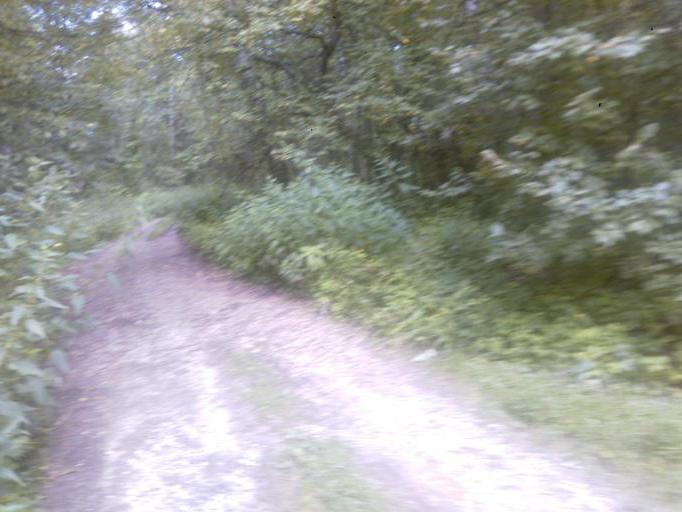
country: RU
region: Moskovskaya
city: Solnechnogorsk
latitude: 56.1373
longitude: 36.9291
